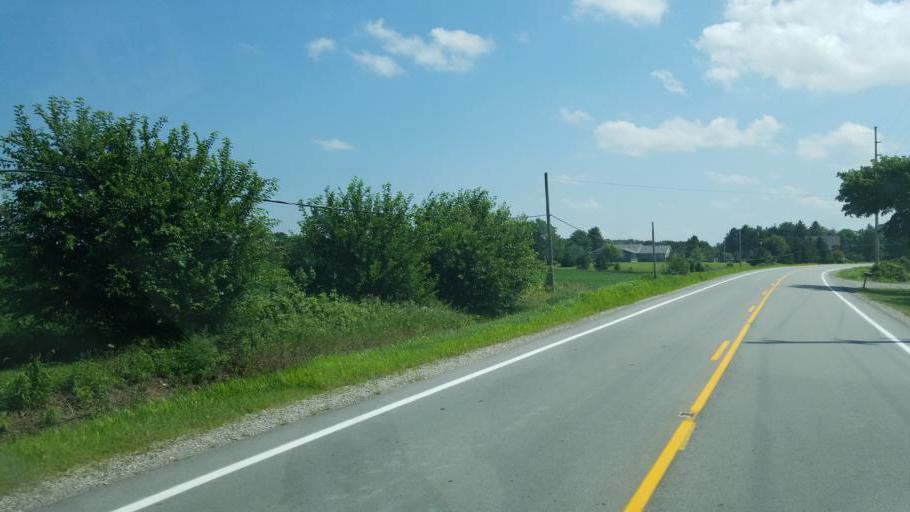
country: US
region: Ohio
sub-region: Huron County
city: Bellevue
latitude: 41.3049
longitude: -82.8292
